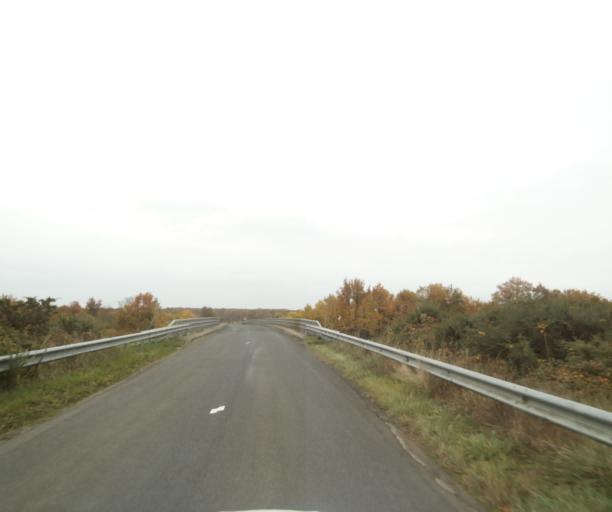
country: FR
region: Poitou-Charentes
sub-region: Departement de la Charente-Maritime
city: Chermignac
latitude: 45.7131
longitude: -0.6941
